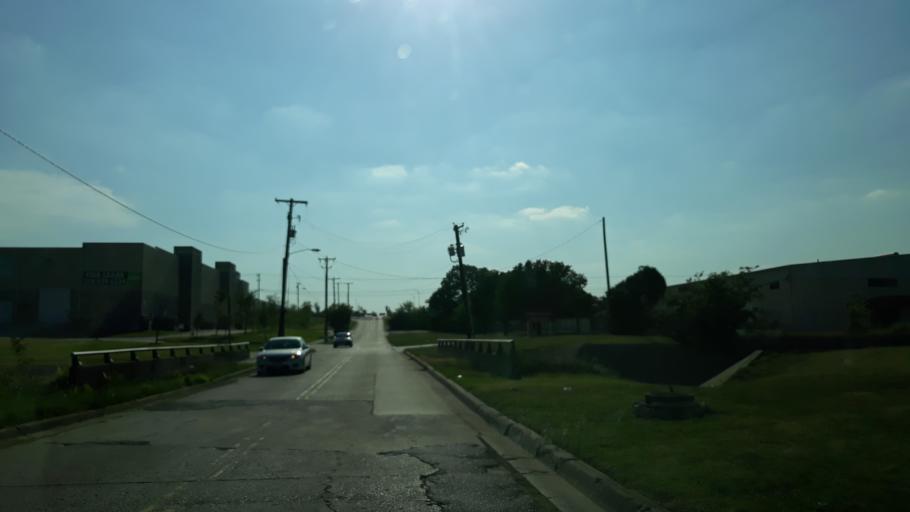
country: US
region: Texas
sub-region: Tarrant County
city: Euless
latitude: 32.8454
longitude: -97.0192
